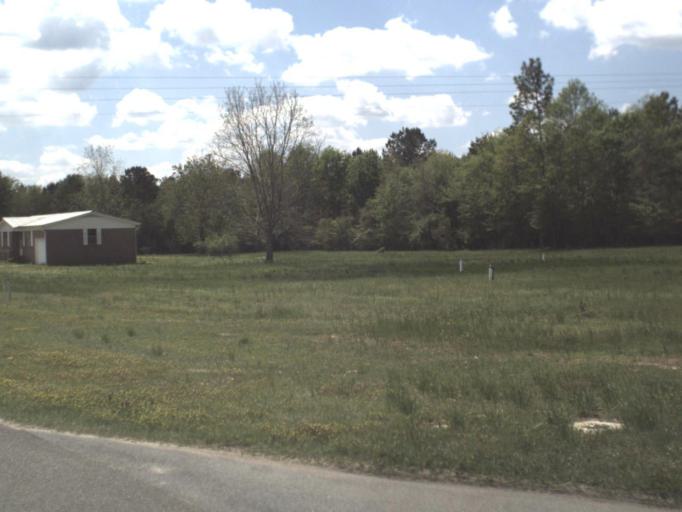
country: US
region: Florida
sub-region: Okaloosa County
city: Crestview
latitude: 30.9579
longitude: -86.6328
